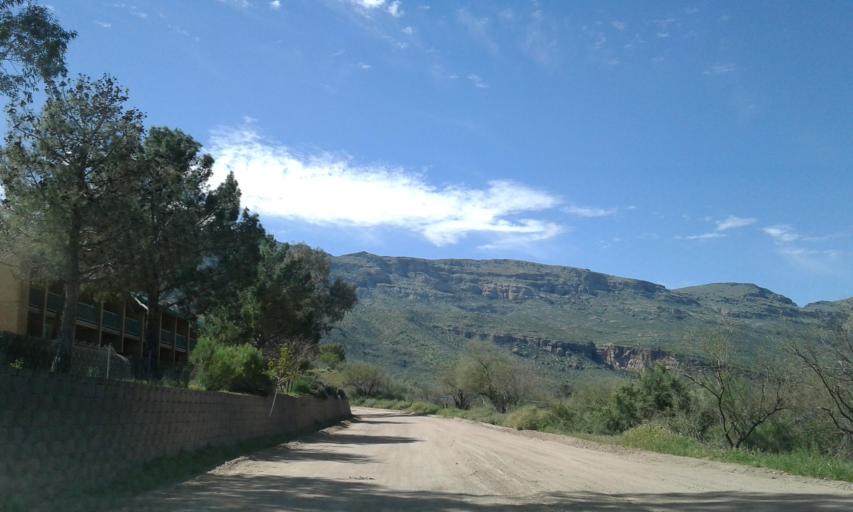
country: US
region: Arizona
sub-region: Gila County
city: Tonto Basin
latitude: 33.5780
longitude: -111.2515
